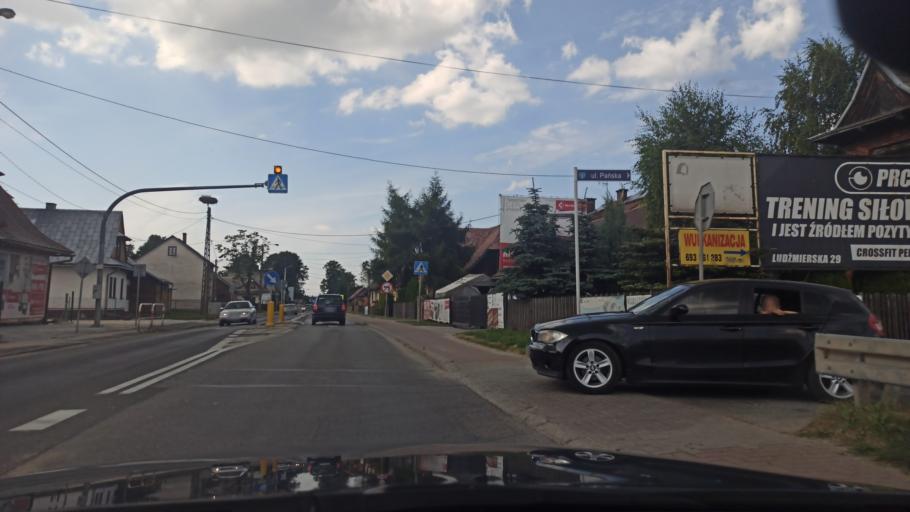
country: PL
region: Lesser Poland Voivodeship
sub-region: Powiat nowotarski
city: Ostrowsko
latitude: 49.4755
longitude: 20.1009
